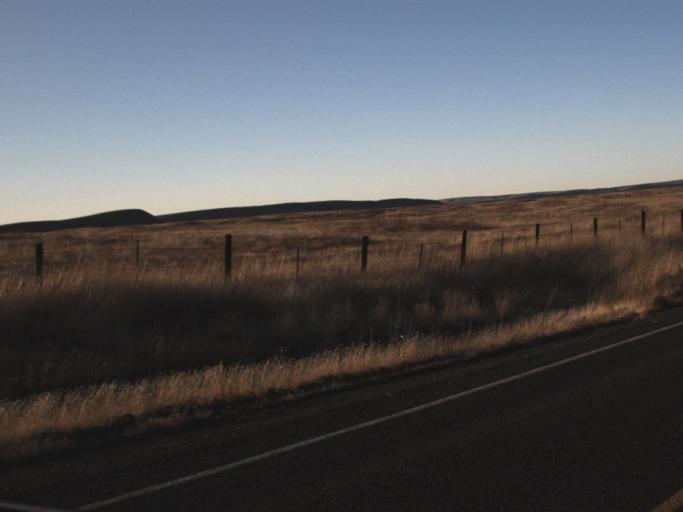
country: US
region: Washington
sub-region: Walla Walla County
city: Waitsburg
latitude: 46.6490
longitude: -118.2555
